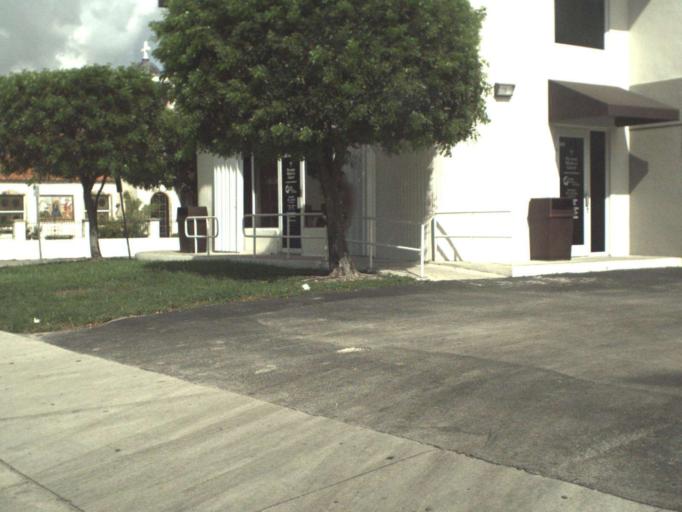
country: US
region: Florida
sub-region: Miami-Dade County
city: West Miami
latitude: 25.7715
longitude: -80.2734
